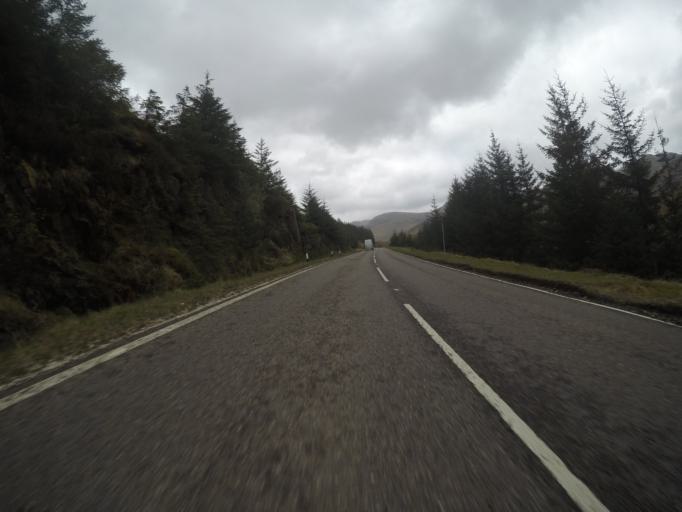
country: GB
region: Scotland
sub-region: Highland
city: Fort William
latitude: 57.1590
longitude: -5.2601
